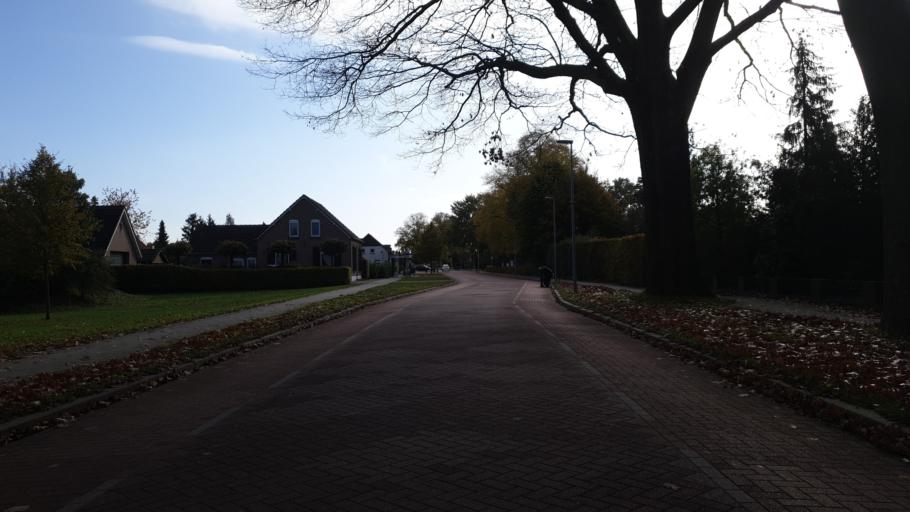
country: NL
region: Limburg
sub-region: Gemeente Gennep
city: Gennep
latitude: 51.6771
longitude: 5.9757
